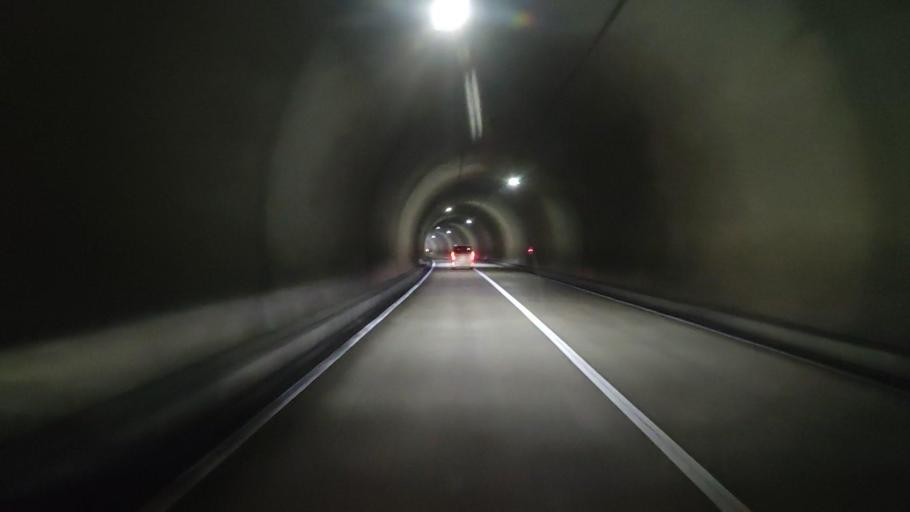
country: JP
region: Wakayama
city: Shingu
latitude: 33.8859
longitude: 135.8792
